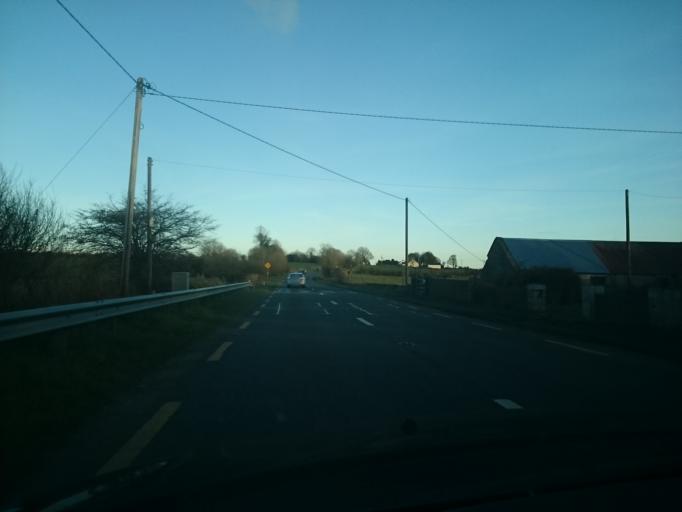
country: IE
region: Connaught
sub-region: Maigh Eo
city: Claremorris
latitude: 53.7634
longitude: -9.0461
